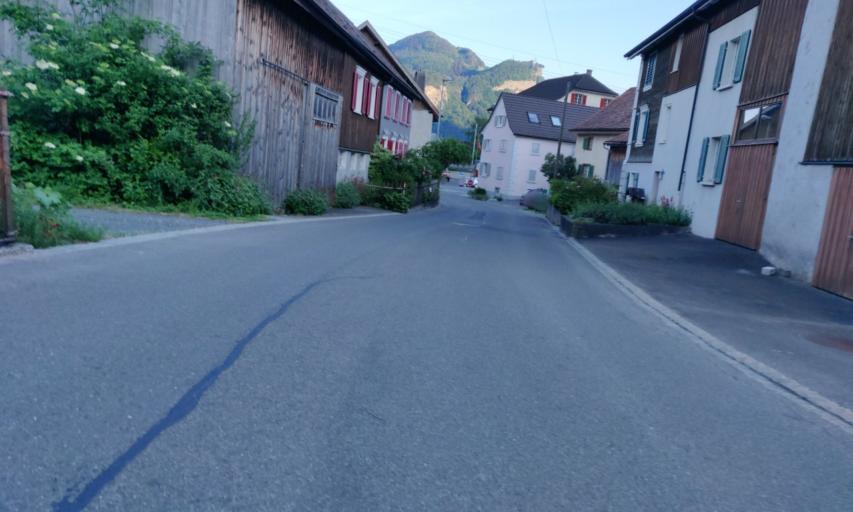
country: LI
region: Balzers
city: Balzers
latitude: 47.0712
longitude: 9.4773
